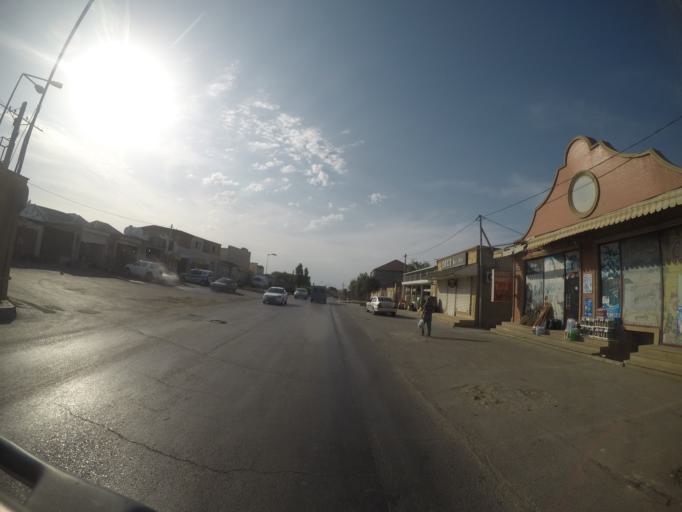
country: AZ
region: Baki
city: Binagadi
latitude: 40.4710
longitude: 49.8372
